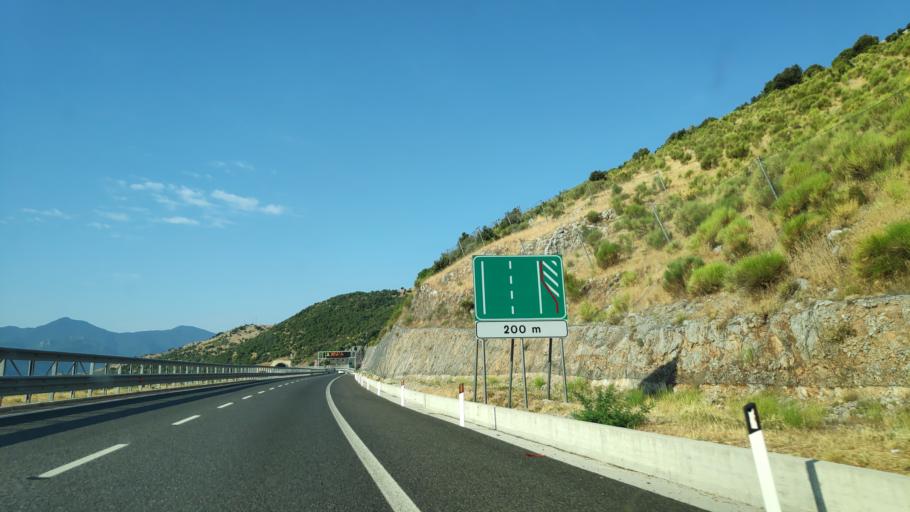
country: IT
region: Calabria
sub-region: Provincia di Cosenza
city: Morano Calabro
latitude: 39.8827
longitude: 16.1322
